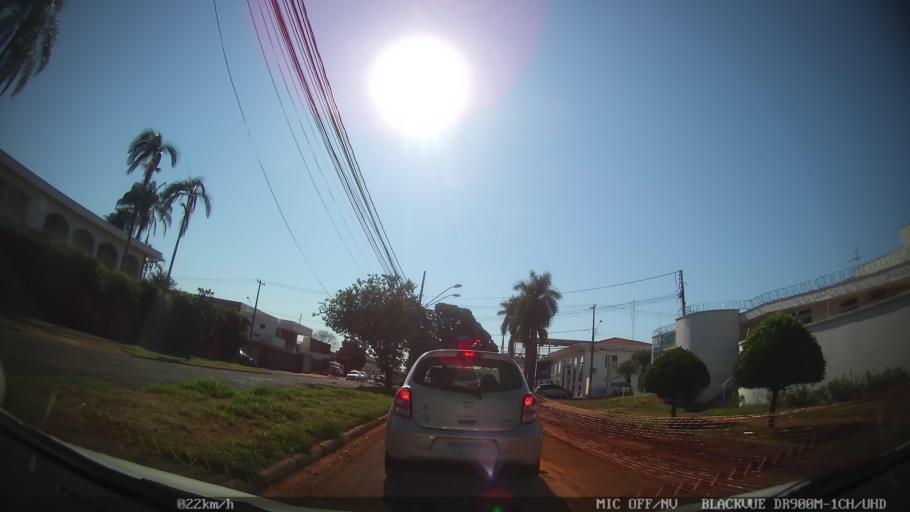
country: BR
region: Sao Paulo
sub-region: Ribeirao Preto
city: Ribeirao Preto
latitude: -21.1948
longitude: -47.8126
